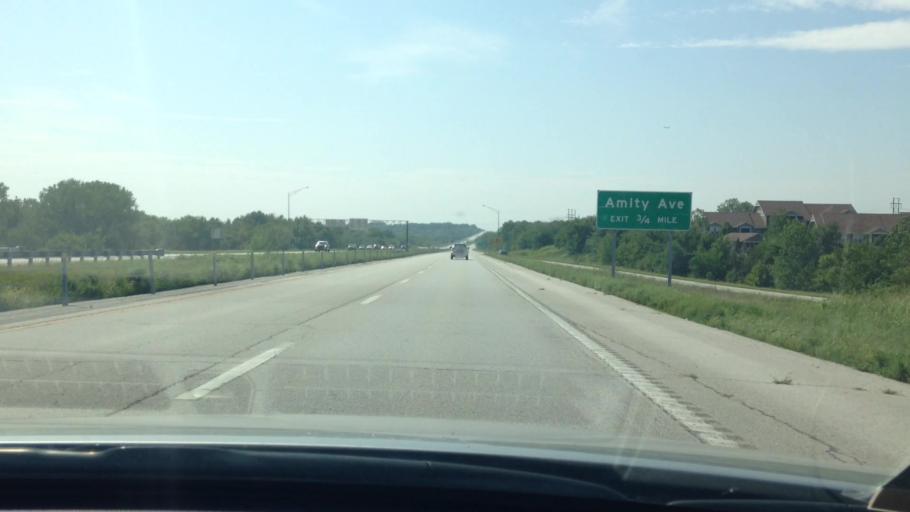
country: US
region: Missouri
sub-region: Platte County
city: Weatherby Lake
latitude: 39.2545
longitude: -94.6688
